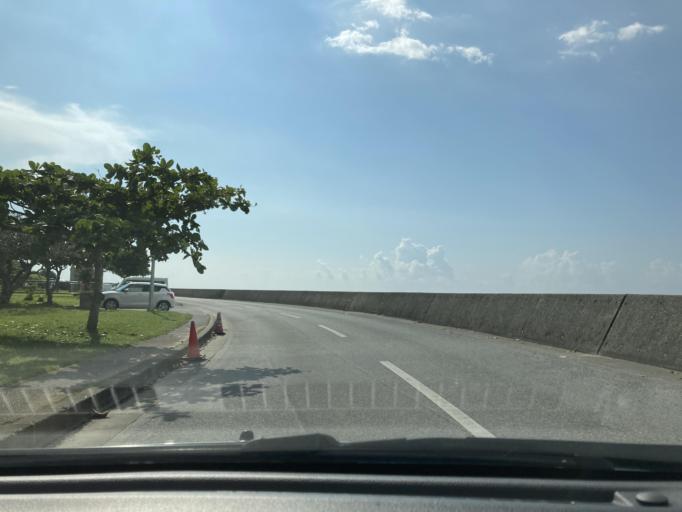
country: JP
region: Okinawa
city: Itoman
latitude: 26.1280
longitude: 127.7713
